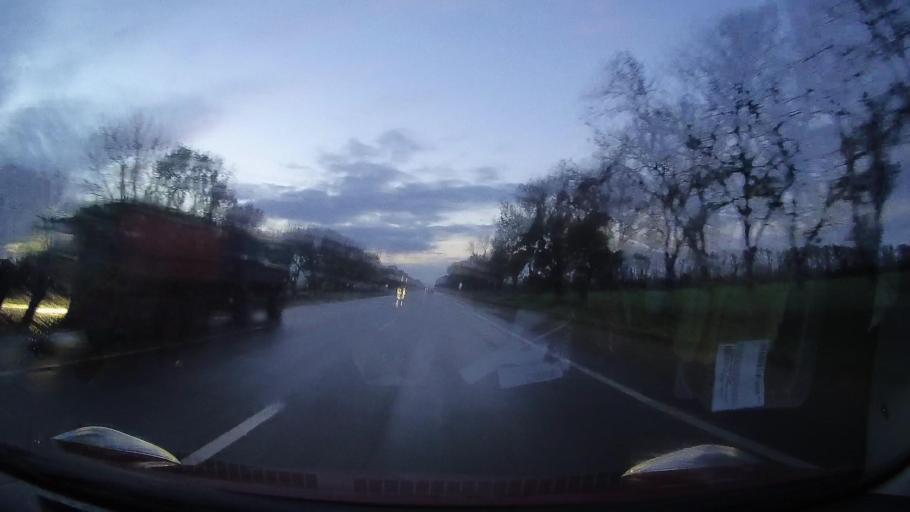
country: RU
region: Krasnodarskiy
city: Zavetnyy
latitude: 44.8886
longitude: 41.2115
